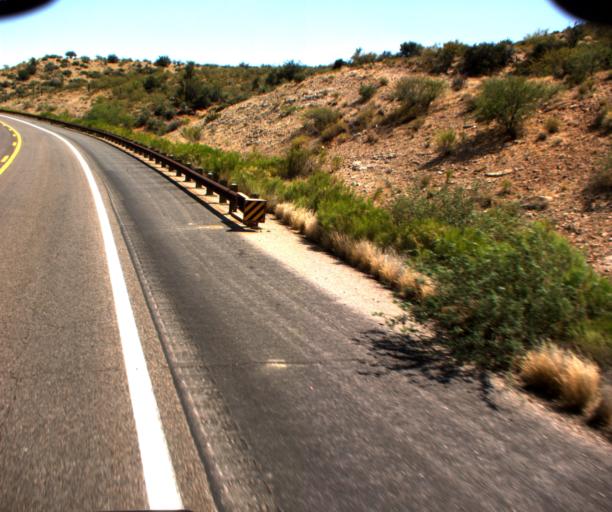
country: US
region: Arizona
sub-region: Gila County
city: Claypool
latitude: 33.4965
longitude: -110.8657
